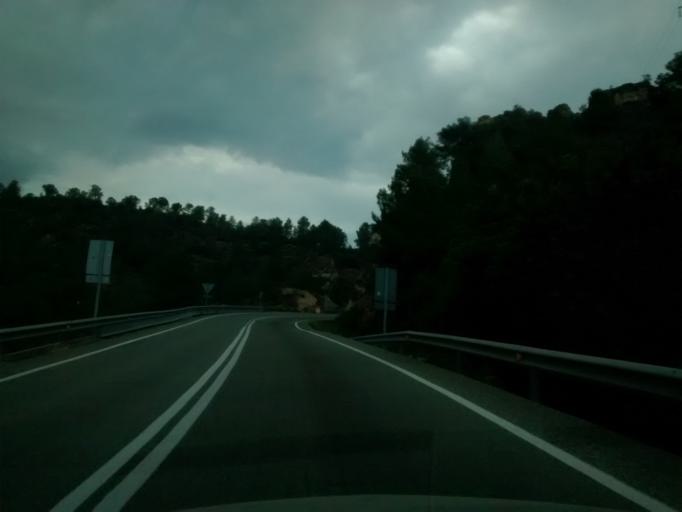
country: ES
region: Catalonia
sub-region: Provincia de Tarragona
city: Benifallet
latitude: 40.9878
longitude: 0.5134
